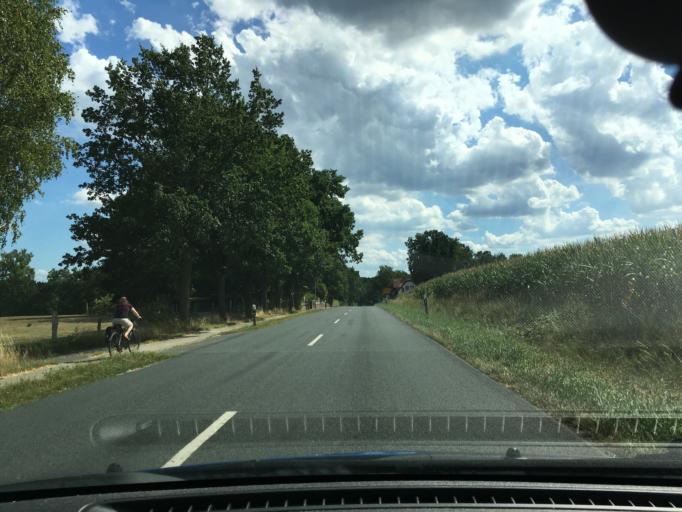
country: DE
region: Lower Saxony
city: Rehlingen
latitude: 53.1107
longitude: 10.2186
